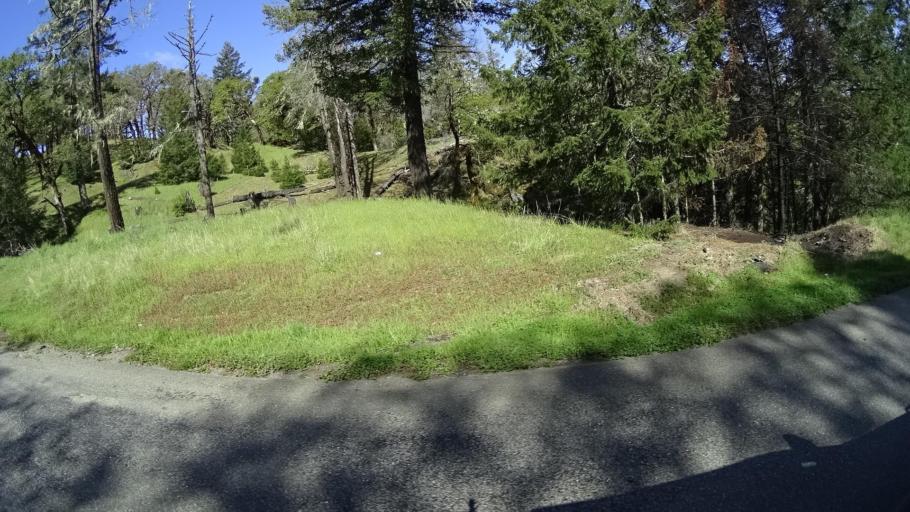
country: US
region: California
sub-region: Humboldt County
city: Redway
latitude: 40.0850
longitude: -123.6655
